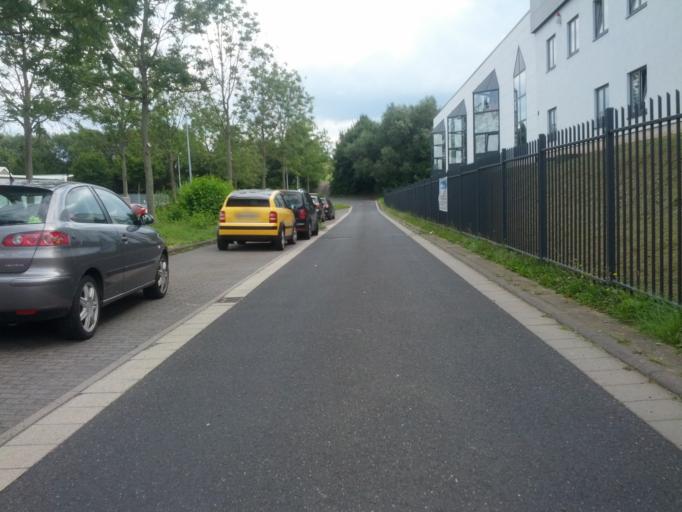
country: DE
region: Thuringia
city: Krauthausen
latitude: 51.0072
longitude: 10.2634
